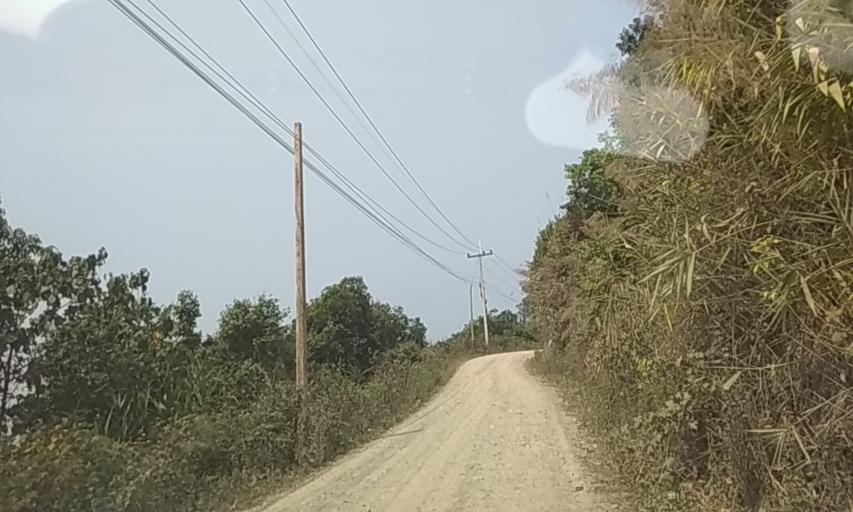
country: TH
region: Nan
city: Chaloem Phra Kiat
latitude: 20.0250
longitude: 101.0989
